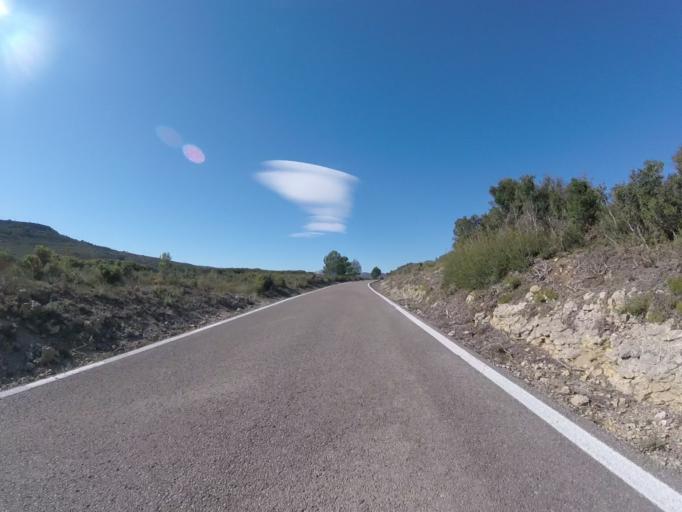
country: ES
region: Valencia
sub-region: Provincia de Castello
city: Albocasser
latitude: 40.3908
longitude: 0.0360
